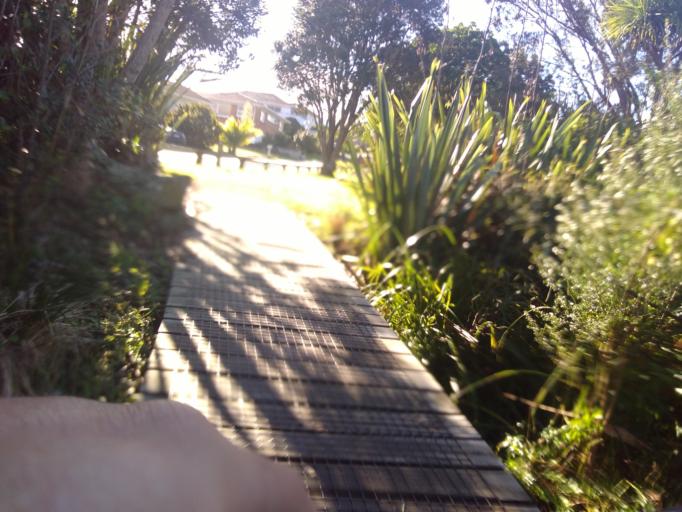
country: NZ
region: Auckland
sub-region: Auckland
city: Rosebank
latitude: -36.8687
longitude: 174.6981
